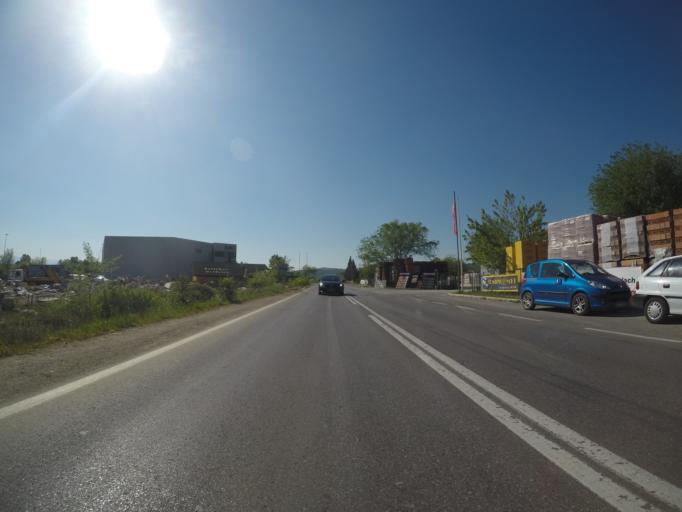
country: ME
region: Danilovgrad
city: Danilovgrad
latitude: 42.5318
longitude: 19.1156
